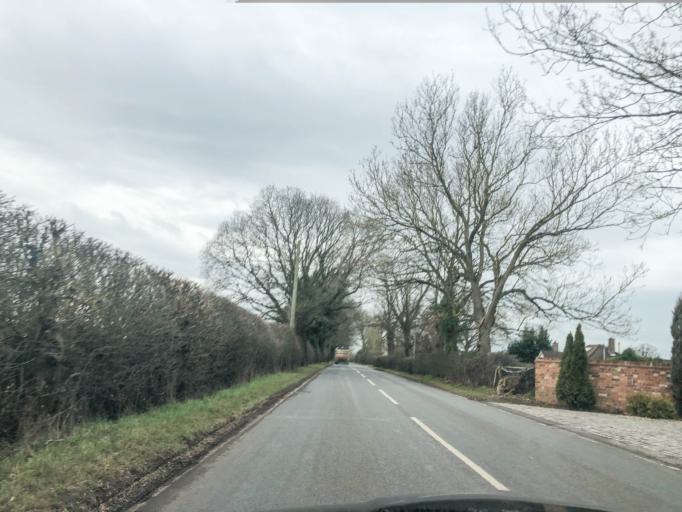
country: GB
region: England
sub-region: Warwickshire
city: Wroxall
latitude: 52.3116
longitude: -1.6777
